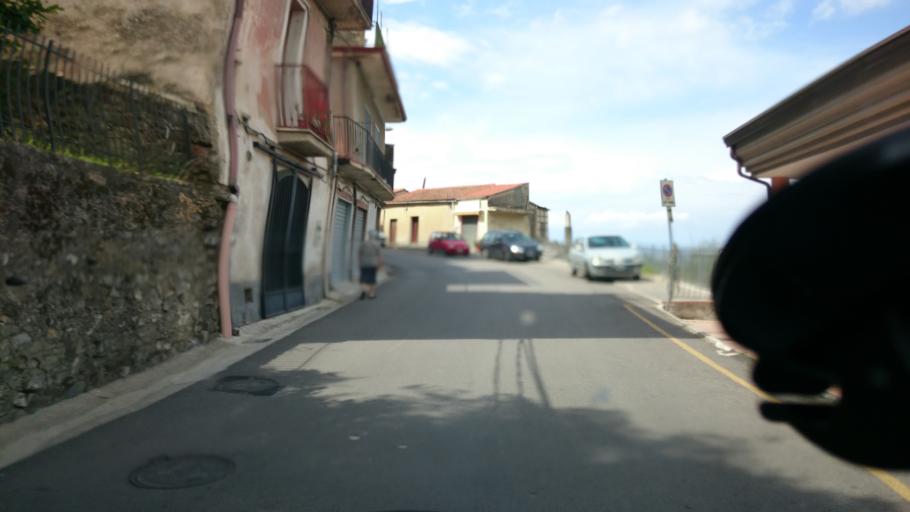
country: IT
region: Campania
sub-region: Provincia di Salerno
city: Pisciotta
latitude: 40.1105
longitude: 15.2333
